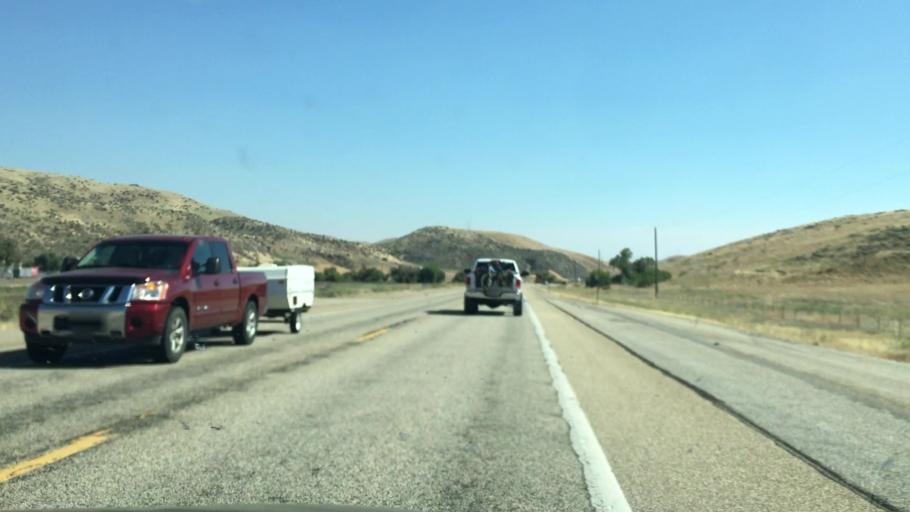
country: US
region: Idaho
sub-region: Ada County
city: Eagle
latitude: 43.7969
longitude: -116.2647
